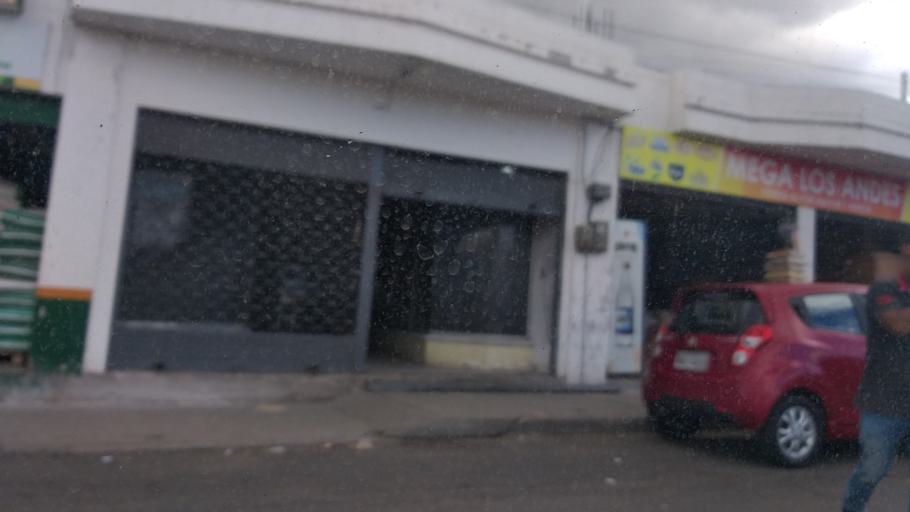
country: EC
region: Chimborazo
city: Riobamba
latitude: -1.6836
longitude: -78.6337
